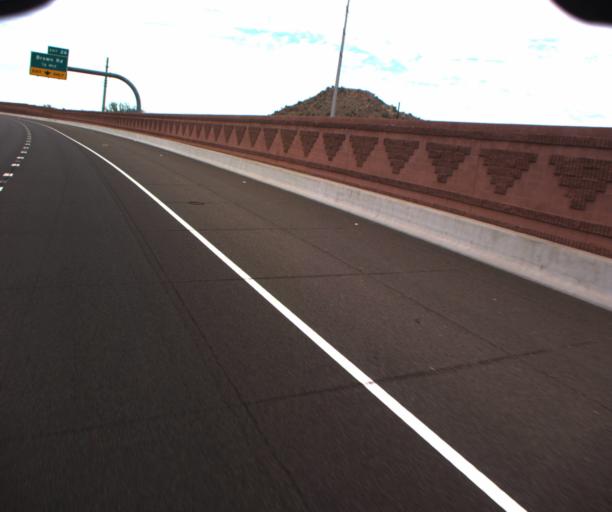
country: US
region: Arizona
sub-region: Pinal County
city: Apache Junction
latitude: 33.4305
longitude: -111.6378
